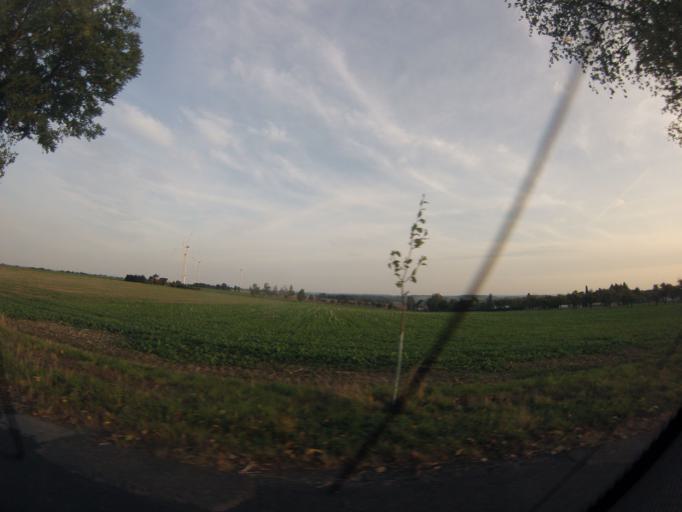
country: DE
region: Thuringia
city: Wildenborten
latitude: 50.9136
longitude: 12.2869
